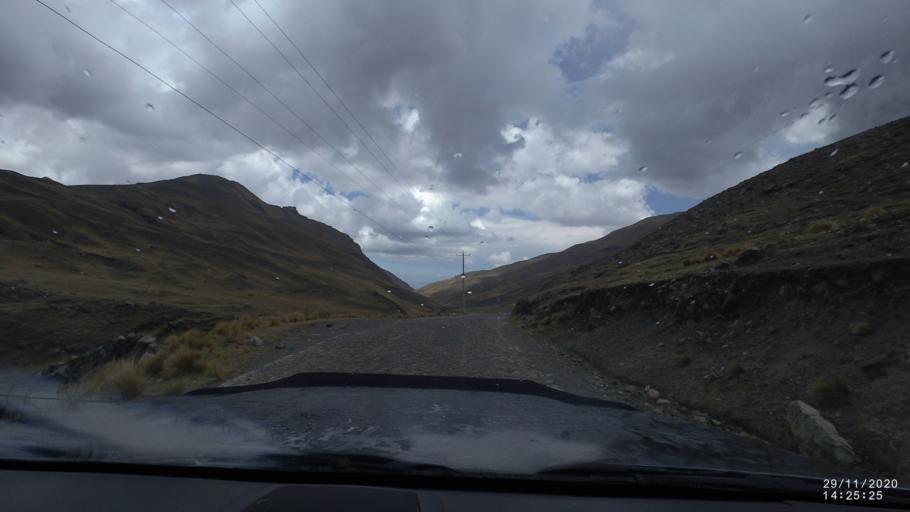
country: BO
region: Cochabamba
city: Sipe Sipe
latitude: -17.2538
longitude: -66.3763
